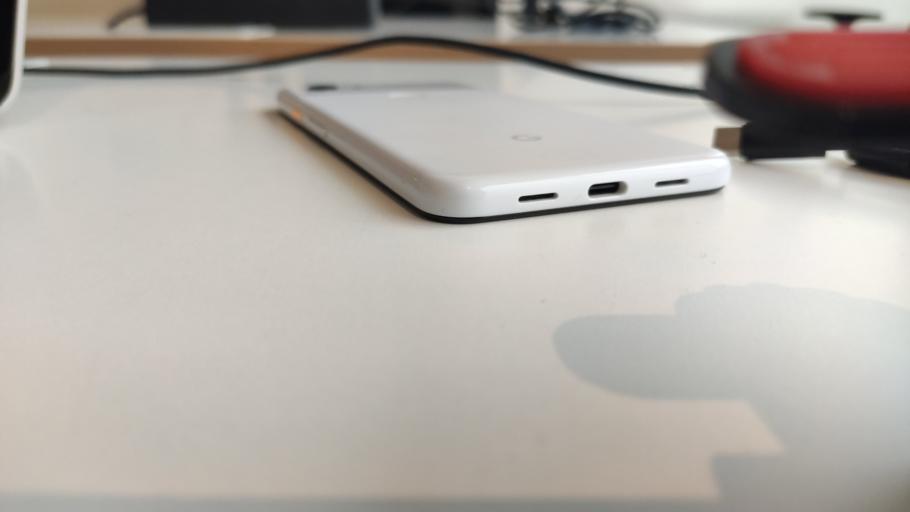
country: RU
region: Moskovskaya
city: Rogachevo
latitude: 56.4319
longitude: 37.1228
